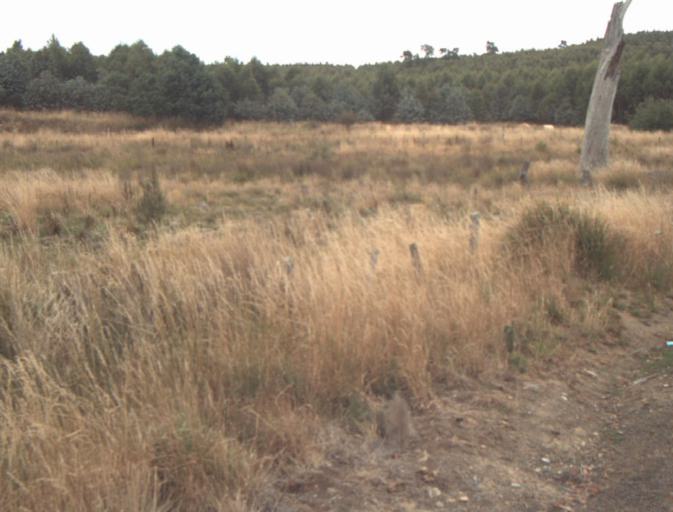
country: AU
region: Tasmania
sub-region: Northern Midlands
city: Evandale
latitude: -41.4771
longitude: 147.5325
